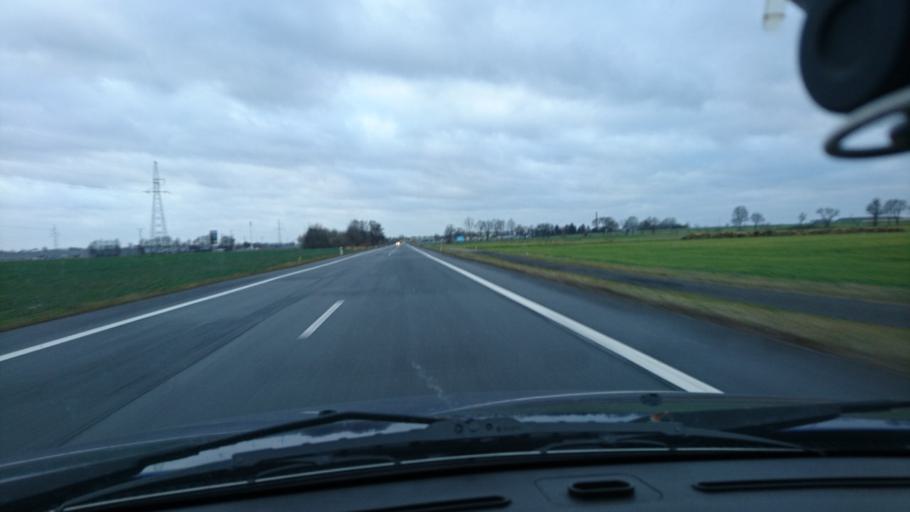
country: PL
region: Opole Voivodeship
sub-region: Powiat kluczborski
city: Kluczbork
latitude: 50.9905
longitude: 18.2226
